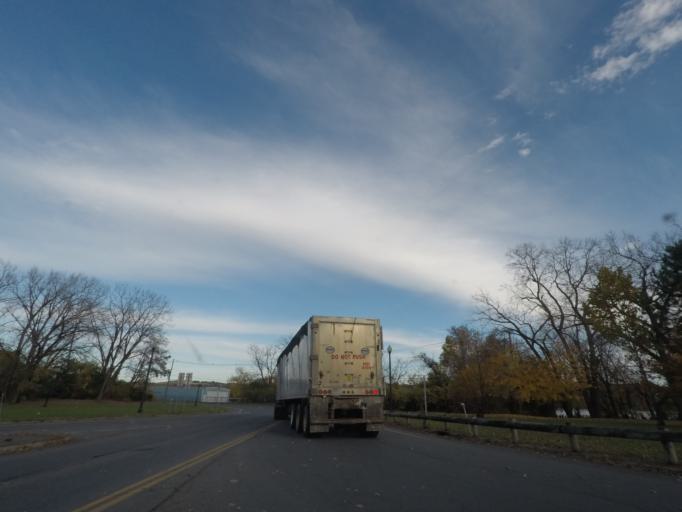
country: US
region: New York
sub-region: Rensselaer County
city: Rensselaer
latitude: 42.6362
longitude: -73.7551
